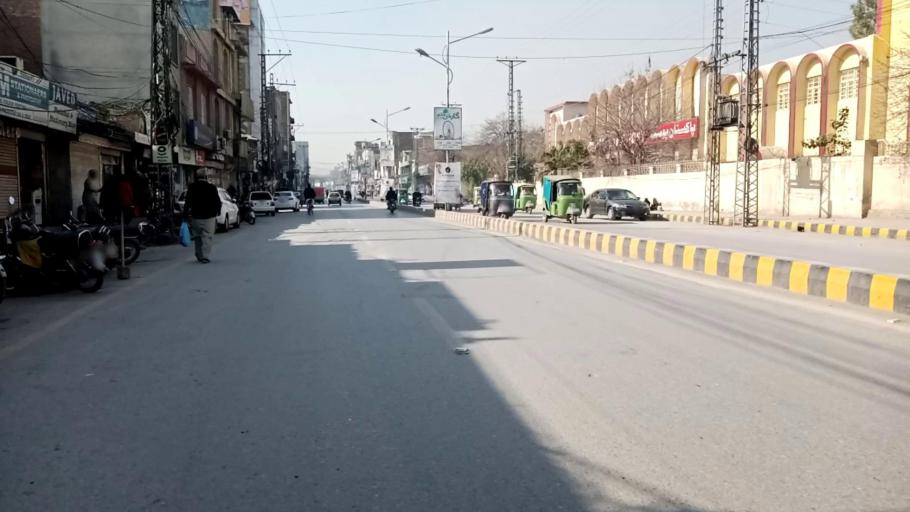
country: PK
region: Khyber Pakhtunkhwa
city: Peshawar
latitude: 34.0000
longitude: 71.5420
